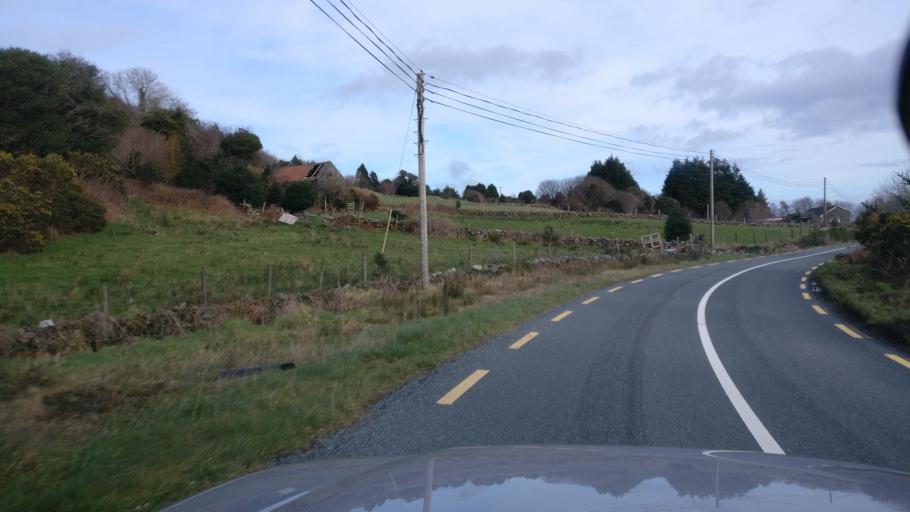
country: IE
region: Connaught
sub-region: County Galway
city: Oughterard
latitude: 53.5167
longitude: -9.4150
